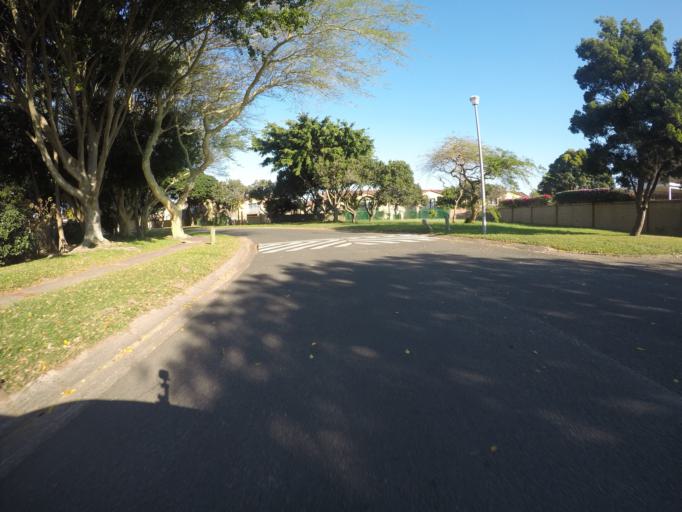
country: ZA
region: KwaZulu-Natal
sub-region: uThungulu District Municipality
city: Richards Bay
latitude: -28.7885
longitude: 32.1004
